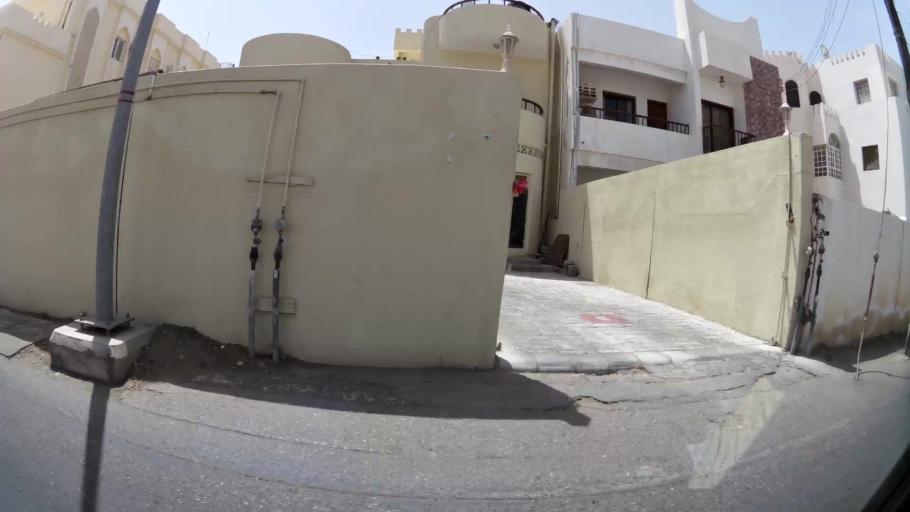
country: OM
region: Muhafazat Masqat
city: Bawshar
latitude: 23.5906
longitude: 58.4327
